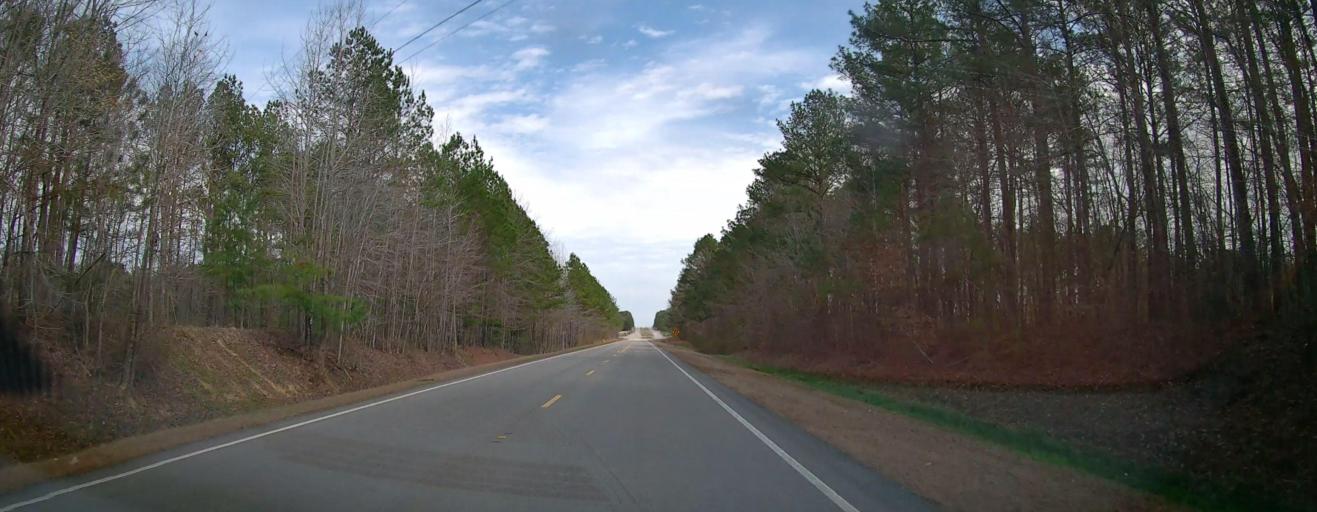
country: US
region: Alabama
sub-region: Marion County
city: Winfield
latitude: 33.9345
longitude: -87.7140
